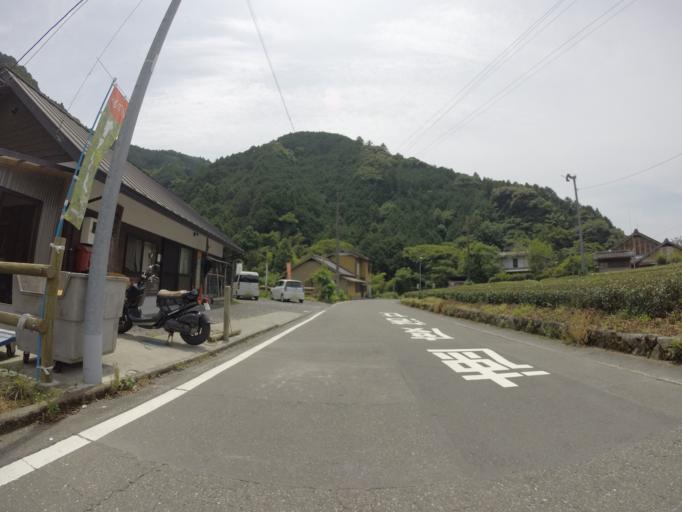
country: JP
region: Shizuoka
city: Shizuoka-shi
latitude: 35.0353
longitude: 138.2929
